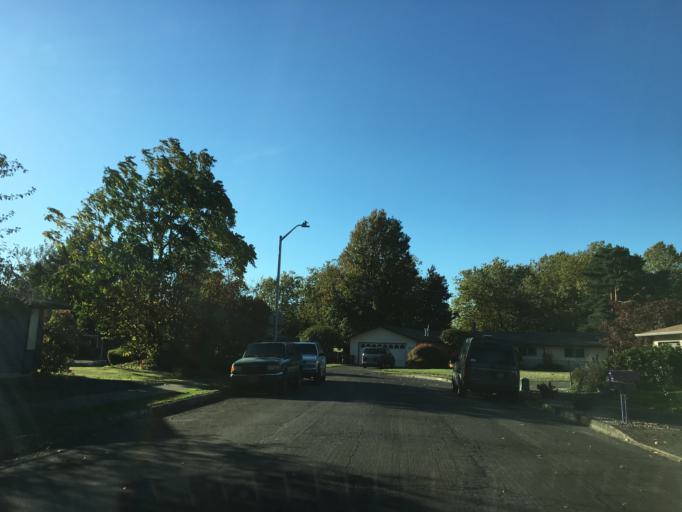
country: US
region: Oregon
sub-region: Multnomah County
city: Wood Village
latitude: 45.5126
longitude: -122.4053
